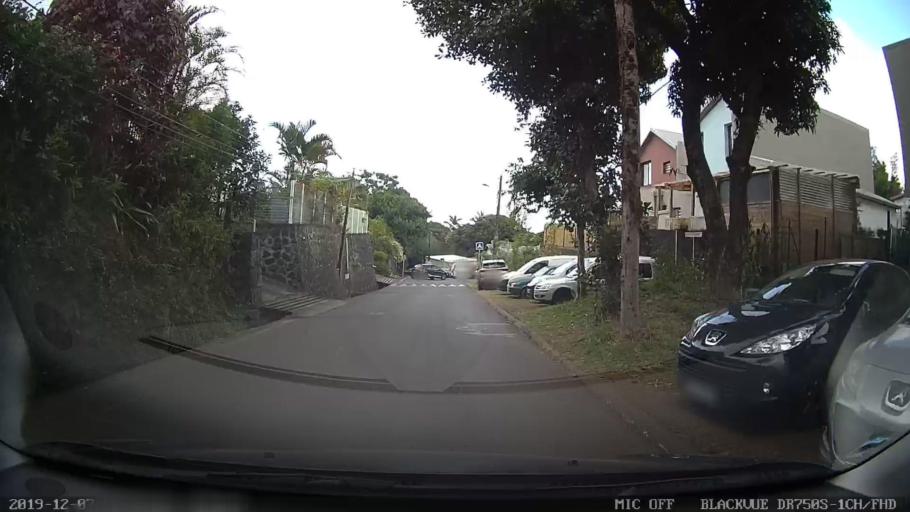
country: RE
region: Reunion
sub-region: Reunion
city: Sainte-Marie
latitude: -20.9341
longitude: 55.5334
